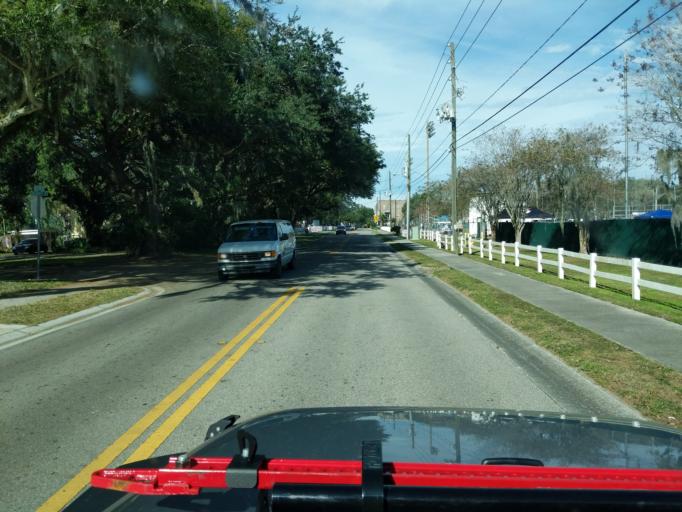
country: US
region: Florida
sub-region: Orange County
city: Winter Garden
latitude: 28.5614
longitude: -81.5919
